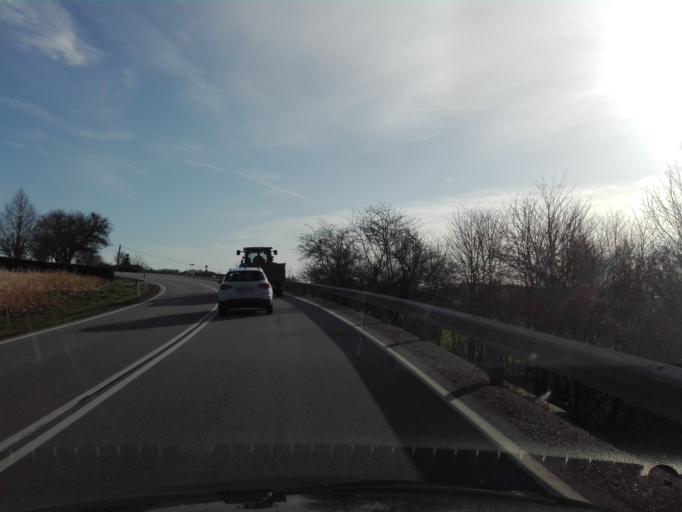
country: AT
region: Lower Austria
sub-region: Politischer Bezirk Amstetten
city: Strengberg
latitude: 48.1374
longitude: 14.6782
